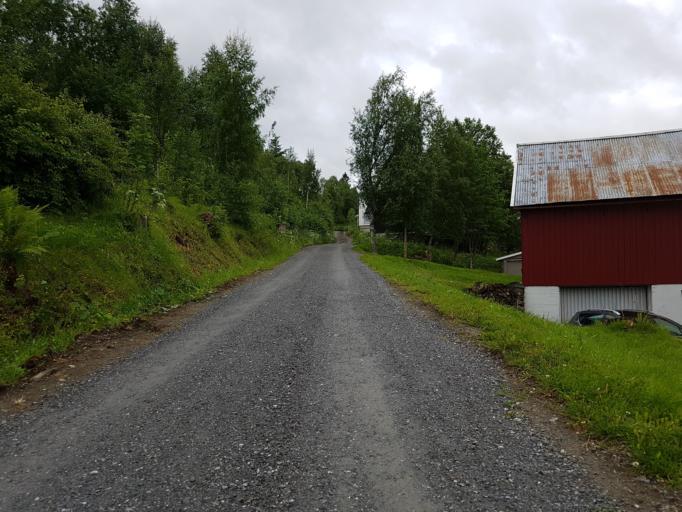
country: NO
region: Sor-Trondelag
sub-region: Selbu
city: Mebonden
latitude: 63.2314
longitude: 11.0345
